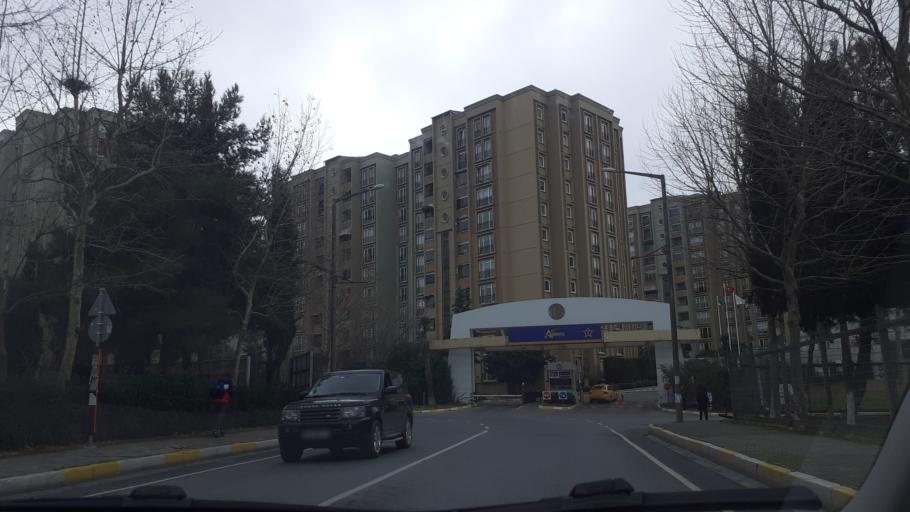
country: TR
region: Istanbul
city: Mahmutbey
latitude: 41.0505
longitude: 28.7870
